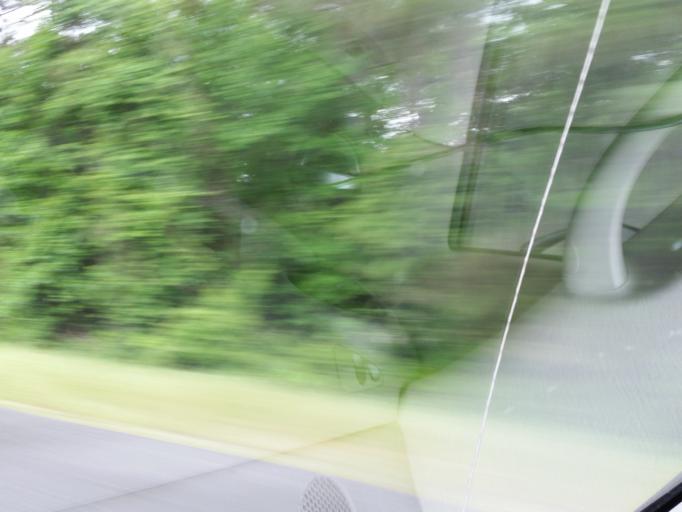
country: US
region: Georgia
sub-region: Houston County
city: Perry
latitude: 32.4008
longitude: -83.7654
